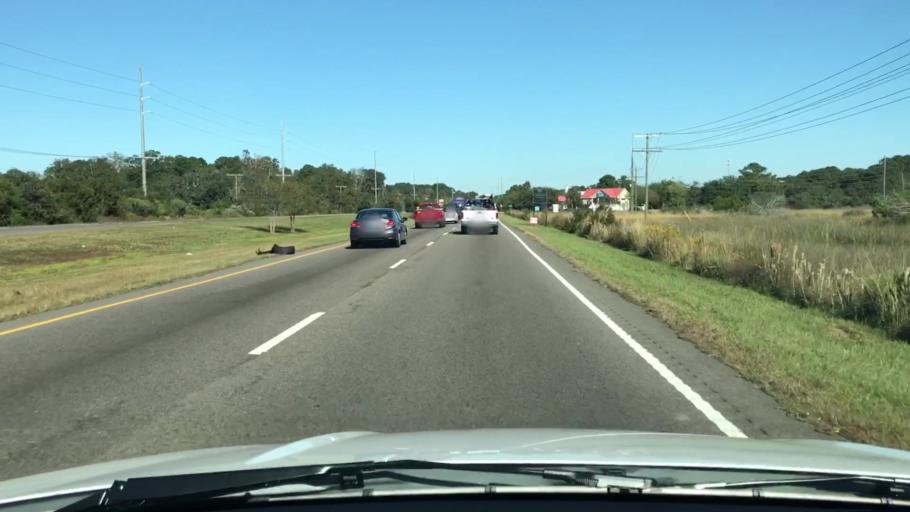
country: US
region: South Carolina
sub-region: Charleston County
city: Shell Point
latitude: 32.7978
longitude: -80.1311
